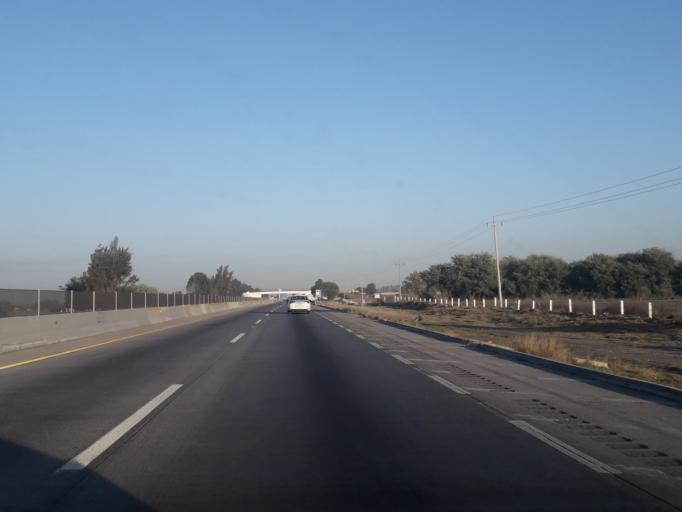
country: MX
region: Puebla
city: San Jeronimo Ocotitlan
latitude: 19.0404
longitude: -97.9996
